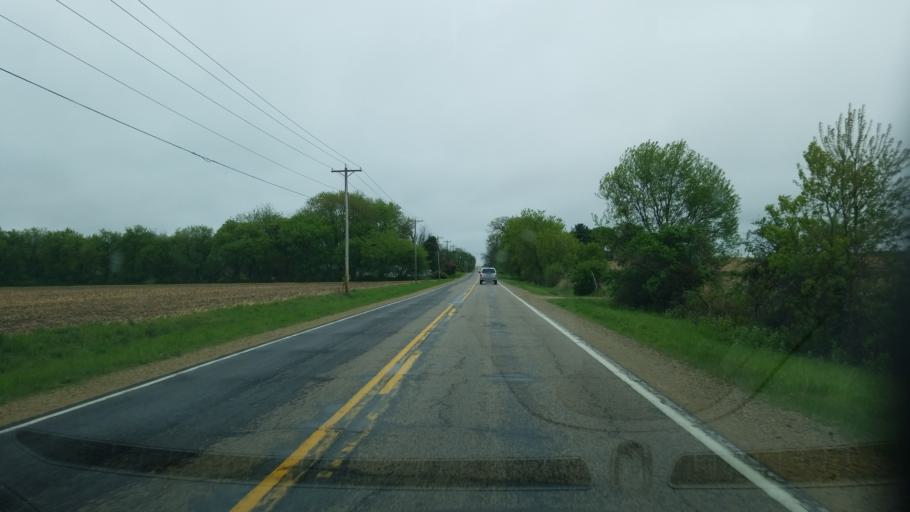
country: US
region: Wisconsin
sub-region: Dane County
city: Oregon
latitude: 42.9292
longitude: -89.4302
